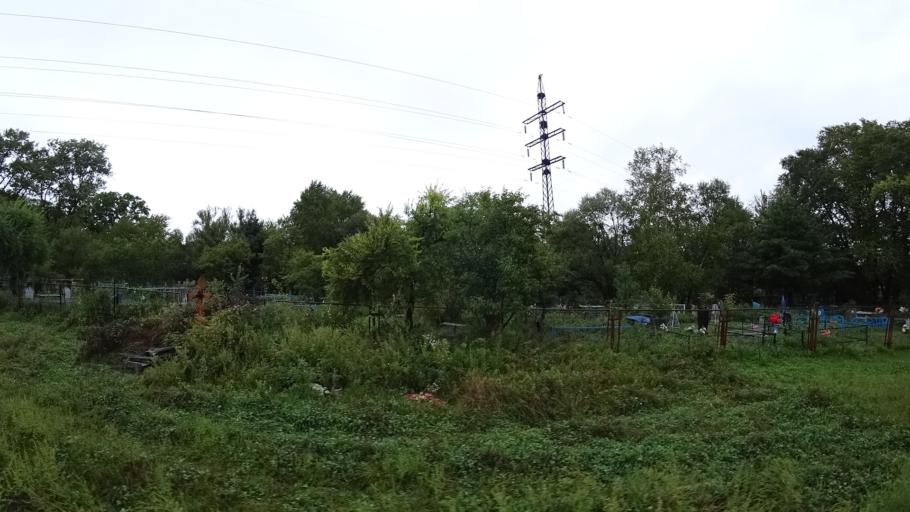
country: RU
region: Primorskiy
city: Monastyrishche
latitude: 44.2635
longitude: 132.4250
